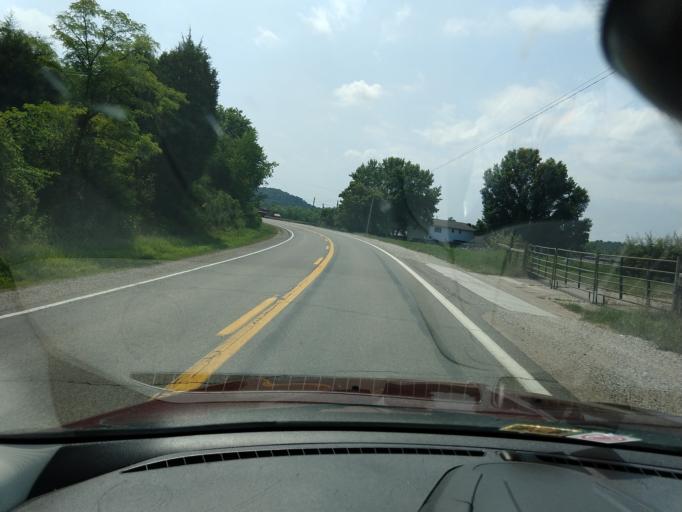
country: US
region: West Virginia
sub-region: Jackson County
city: Ravenswood
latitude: 38.8720
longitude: -81.8253
